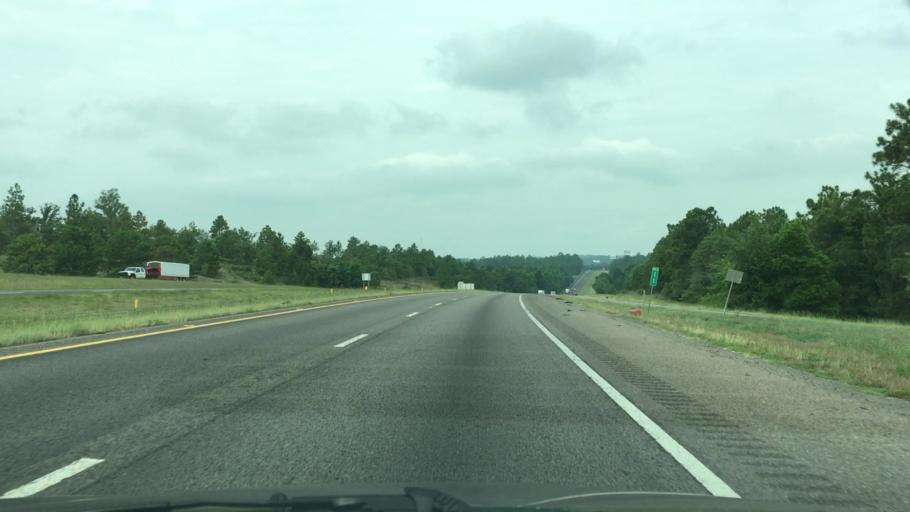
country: US
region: South Carolina
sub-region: Aiken County
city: Graniteville
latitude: 33.6054
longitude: -81.8461
